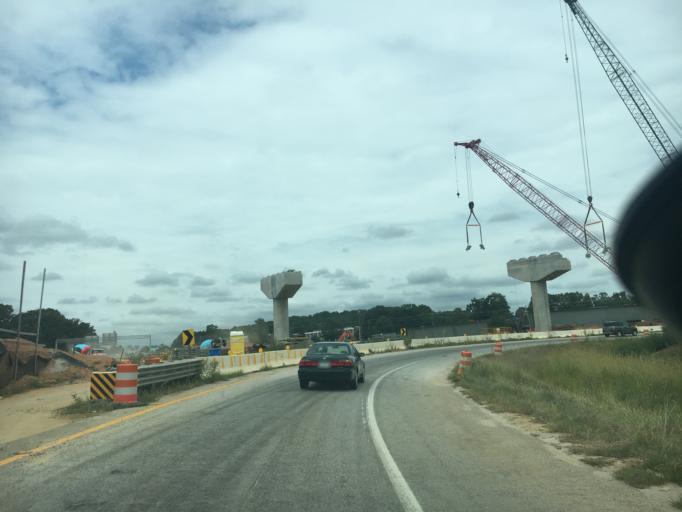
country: US
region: South Carolina
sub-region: Greenville County
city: Mauldin
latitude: 34.8327
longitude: -82.2992
